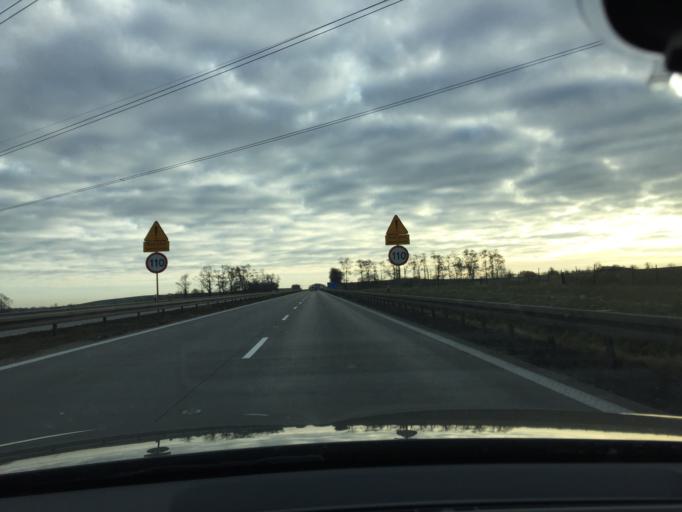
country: PL
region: Lower Silesian Voivodeship
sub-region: Powiat legnicki
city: Legnickie Pole
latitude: 51.1391
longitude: 16.2849
